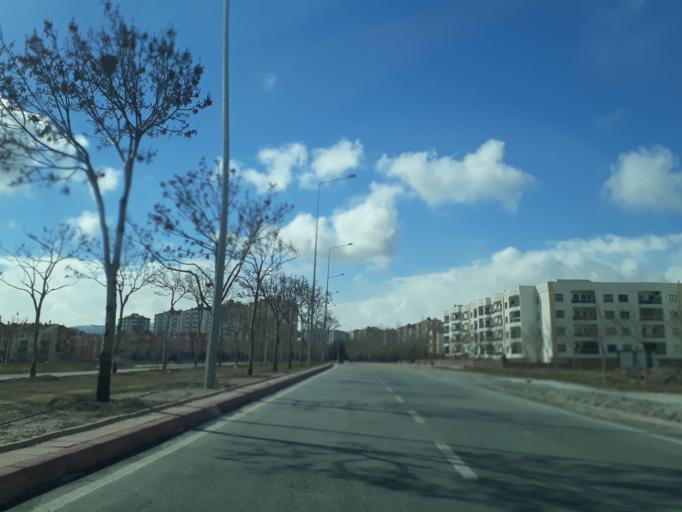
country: TR
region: Konya
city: Asagipinarbasi
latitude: 38.0068
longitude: 32.5396
